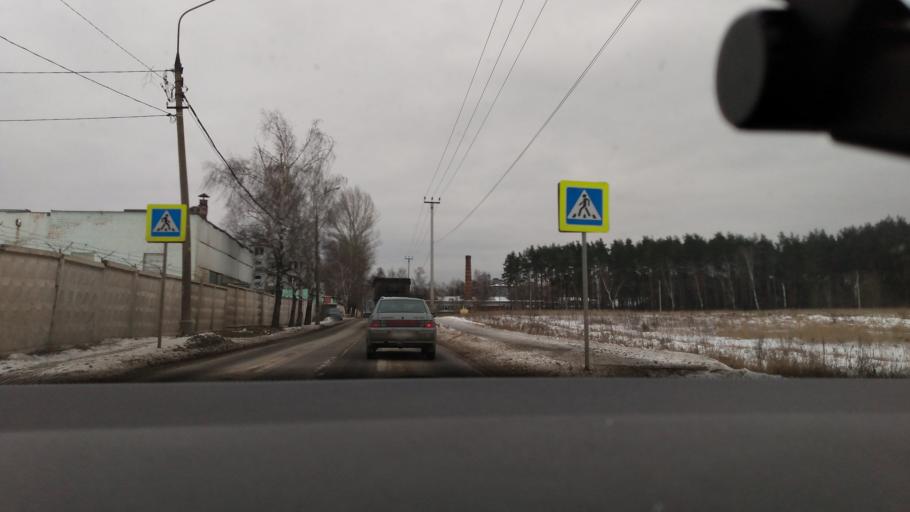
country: RU
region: Moskovskaya
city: Rodniki
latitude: 55.6804
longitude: 38.1009
